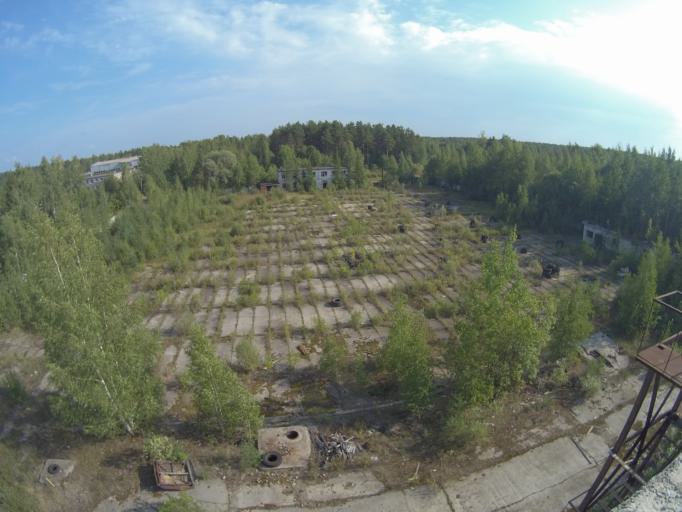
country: RU
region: Vladimir
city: Raduzhnyy
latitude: 55.9786
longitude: 40.2712
